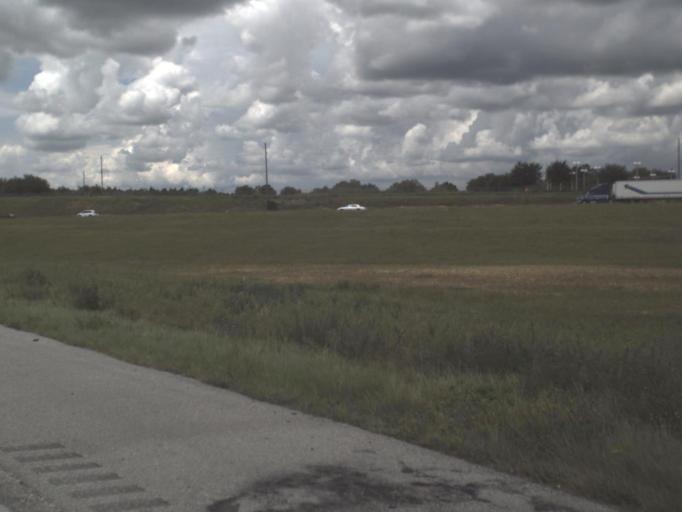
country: US
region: Florida
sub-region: Polk County
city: Davenport
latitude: 28.2311
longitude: -81.6524
